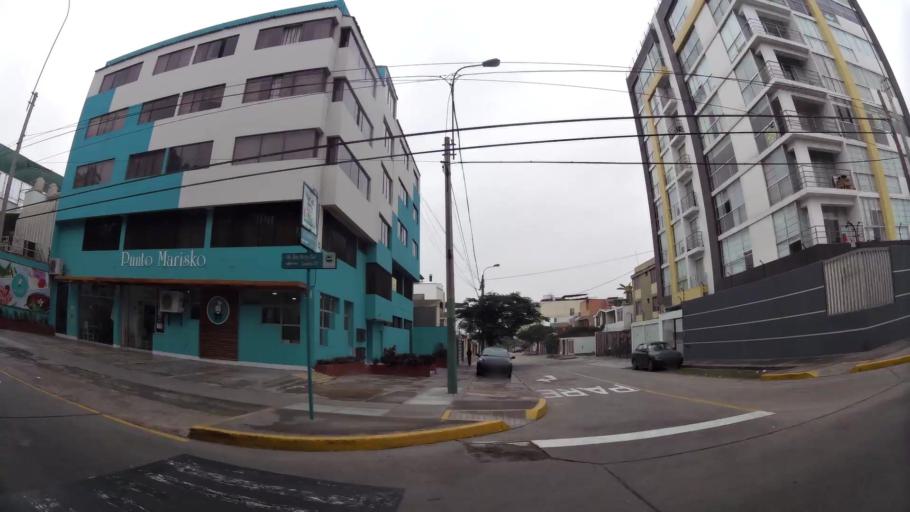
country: PE
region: Lima
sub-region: Lima
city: San Luis
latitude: -12.1009
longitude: -76.9990
